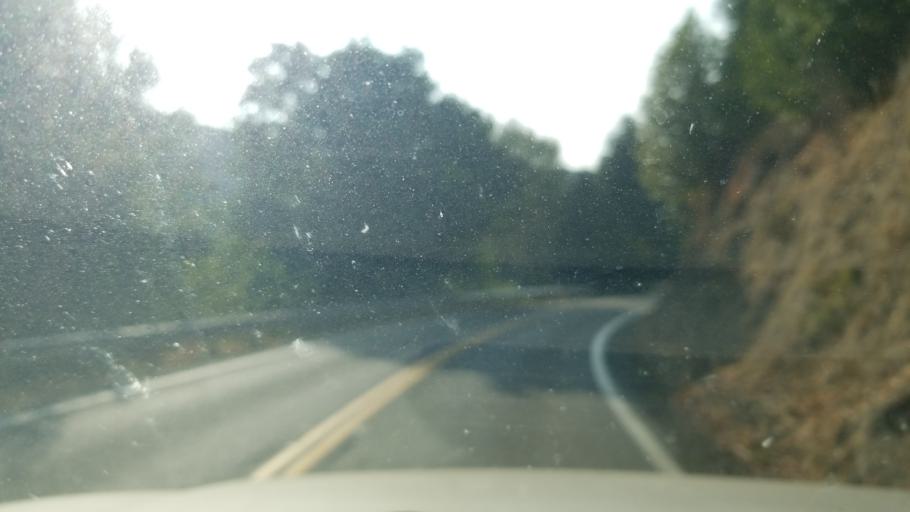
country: US
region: California
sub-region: Humboldt County
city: Redway
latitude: 40.2571
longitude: -123.8293
